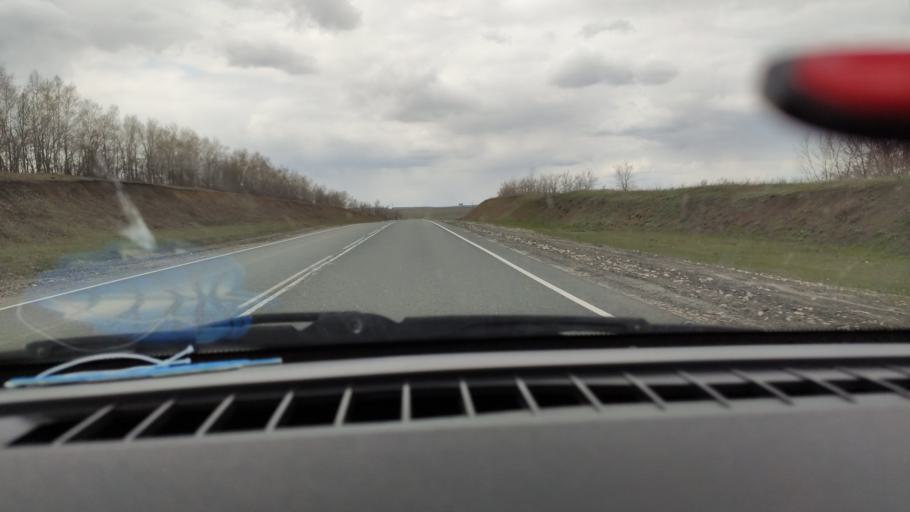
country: RU
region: Saratov
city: Shikhany
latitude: 52.1177
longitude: 47.2781
